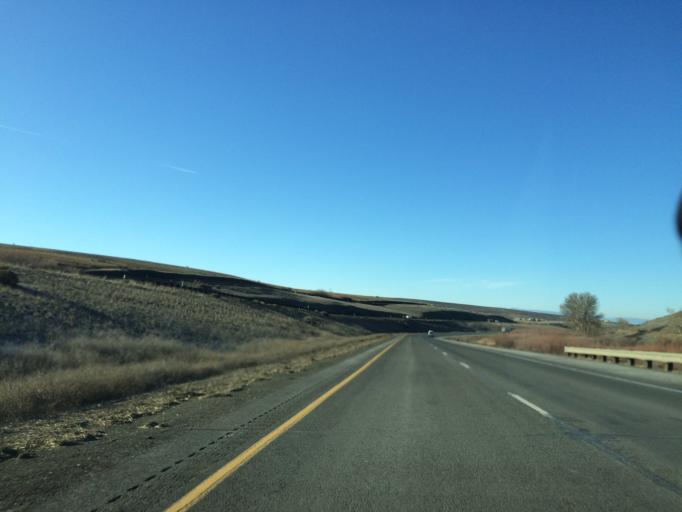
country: US
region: Washington
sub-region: Kittitas County
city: Kittitas
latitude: 46.9584
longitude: -120.3145
